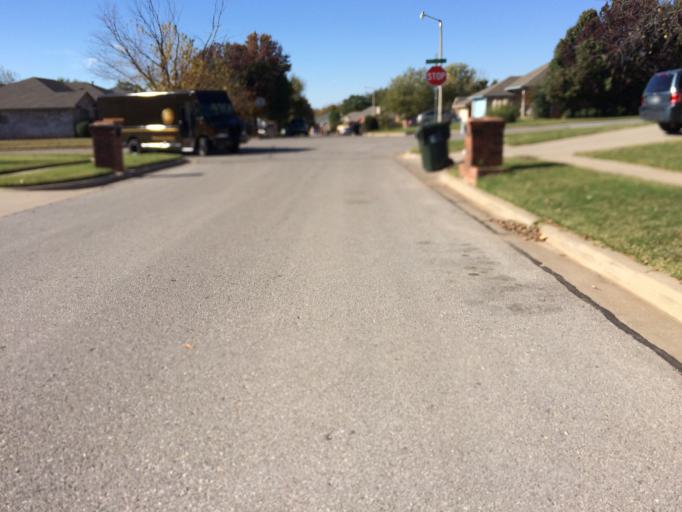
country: US
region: Oklahoma
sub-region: Cleveland County
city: Noble
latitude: 35.1706
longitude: -97.4281
